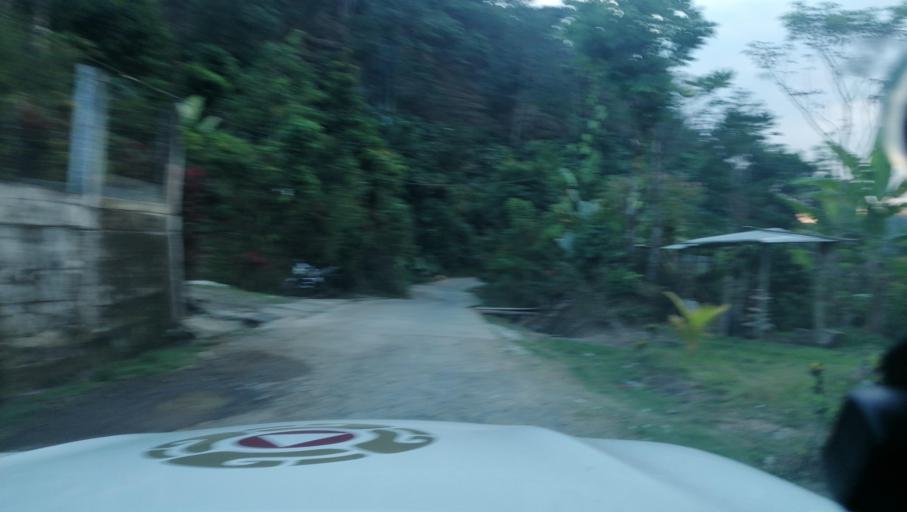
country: MX
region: Chiapas
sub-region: Cacahoatan
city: Benito Juarez
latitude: 15.0695
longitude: -92.2322
